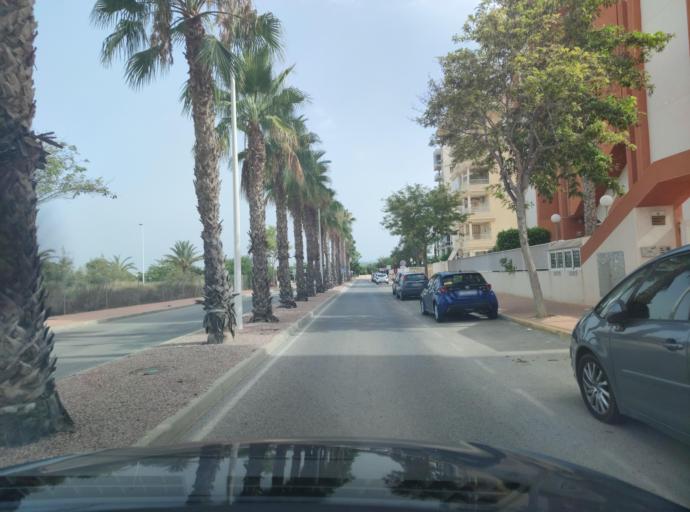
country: ES
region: Valencia
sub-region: Provincia de Alicante
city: Guardamar del Segura
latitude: 38.1020
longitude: -0.6558
